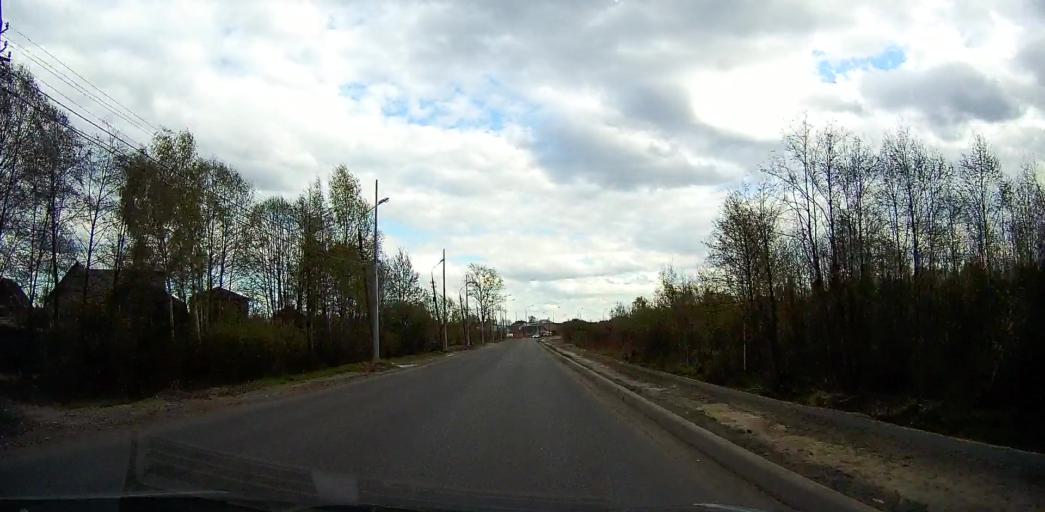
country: RU
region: Moskovskaya
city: Pavlovskiy Posad
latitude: 55.7981
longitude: 38.6877
